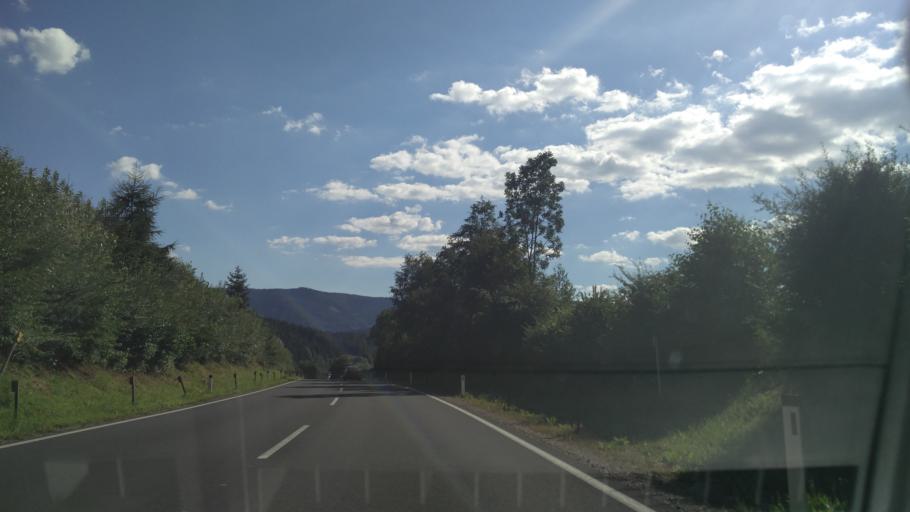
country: AT
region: Styria
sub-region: Politischer Bezirk Leoben
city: Trofaiach
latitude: 47.4115
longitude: 15.0022
